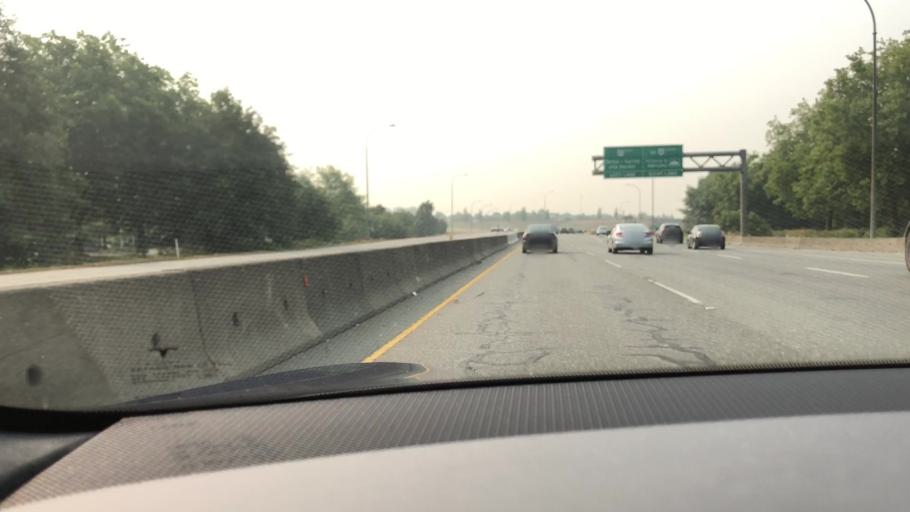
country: CA
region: British Columbia
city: Richmond
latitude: 49.1823
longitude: -123.0762
